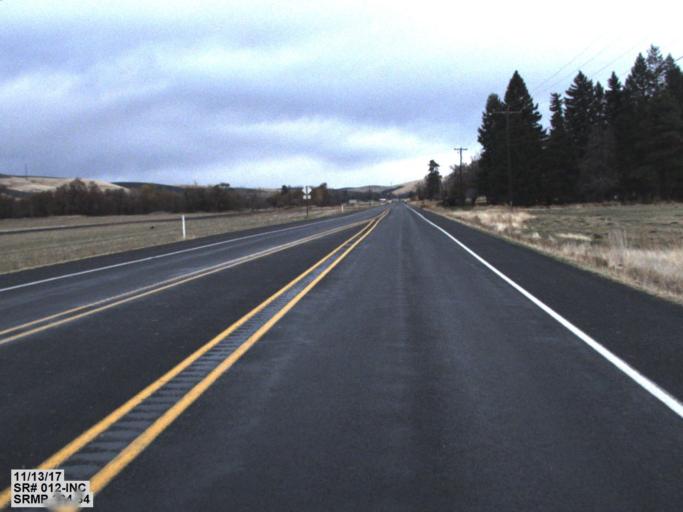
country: US
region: Washington
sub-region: Columbia County
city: Dayton
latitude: 46.2950
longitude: -118.0214
